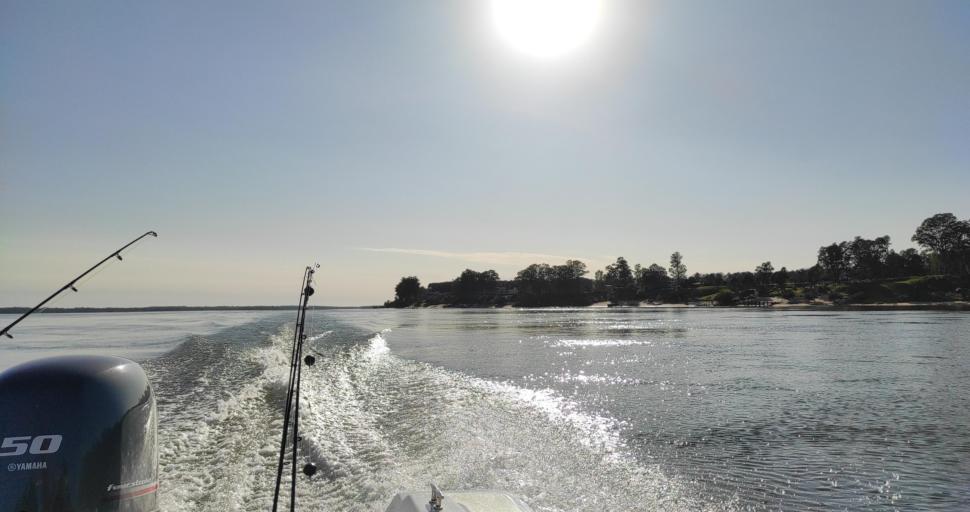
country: AR
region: Corrientes
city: Ituzaingo
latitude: -27.6024
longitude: -56.8222
